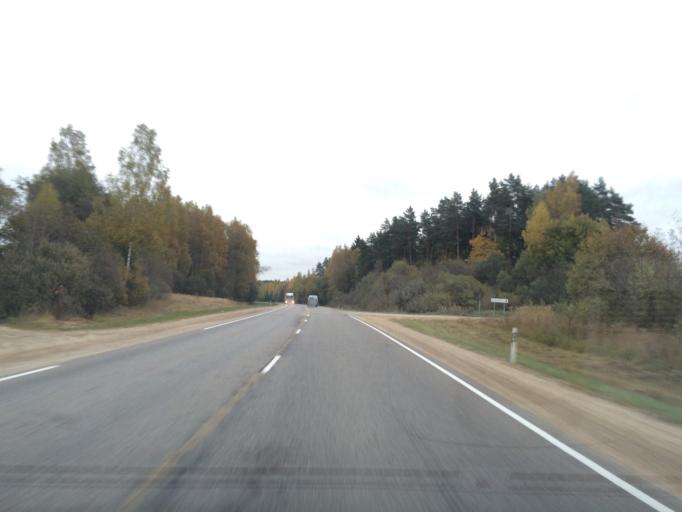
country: LV
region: Koknese
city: Koknese
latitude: 56.5892
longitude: 25.5649
